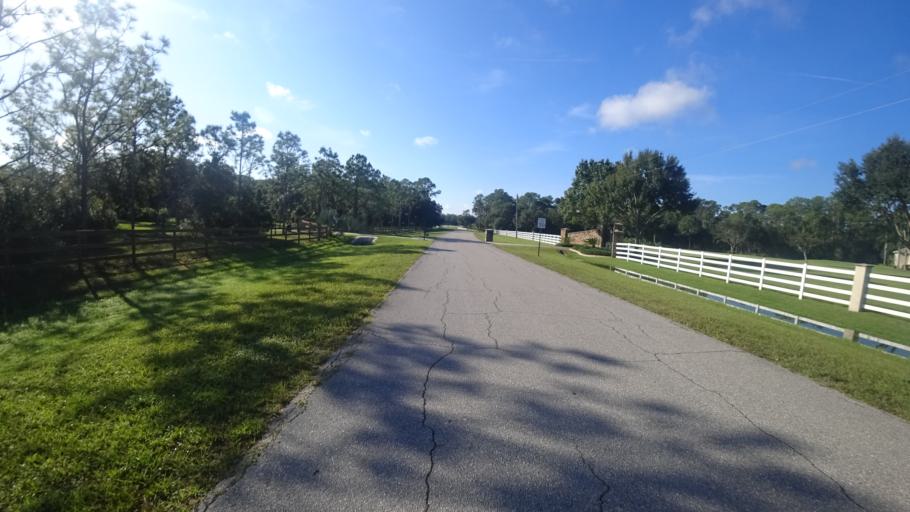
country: US
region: Florida
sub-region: Sarasota County
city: The Meadows
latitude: 27.4223
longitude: -82.3437
